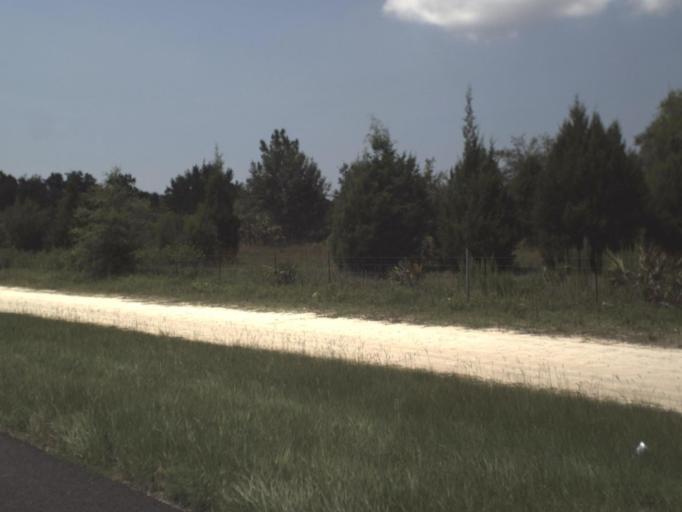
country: US
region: Florida
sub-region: Levy County
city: Inglis
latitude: 29.0079
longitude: -82.6604
